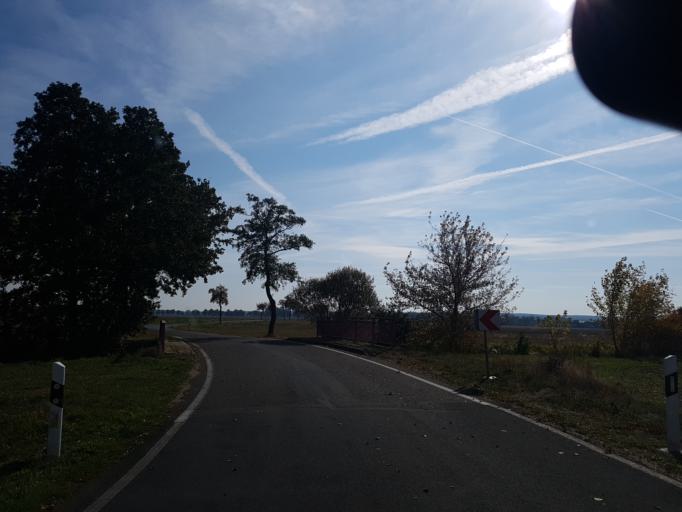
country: DE
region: Brandenburg
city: Ihlow
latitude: 51.8309
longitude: 13.3505
